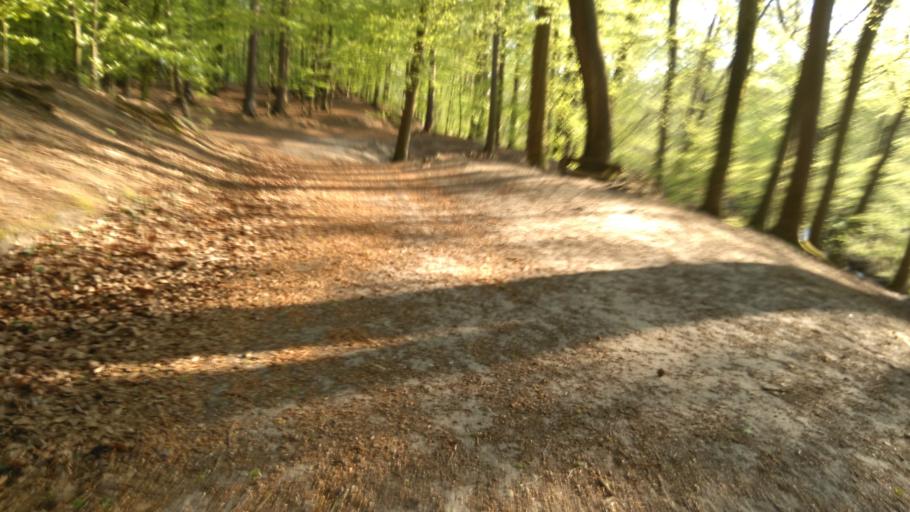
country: DE
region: Lower Saxony
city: Nottensdorf
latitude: 53.4790
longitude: 9.6289
